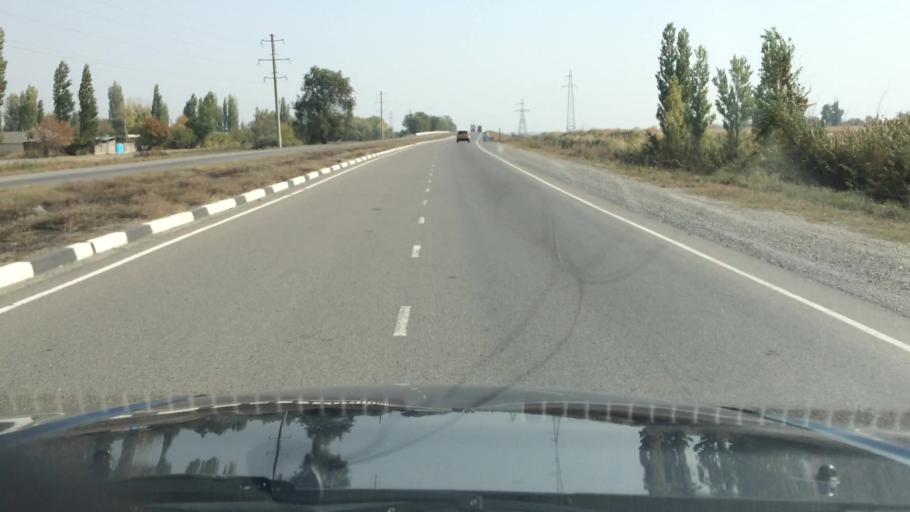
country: KG
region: Chuy
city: Kant
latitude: 42.9675
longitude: 74.8304
